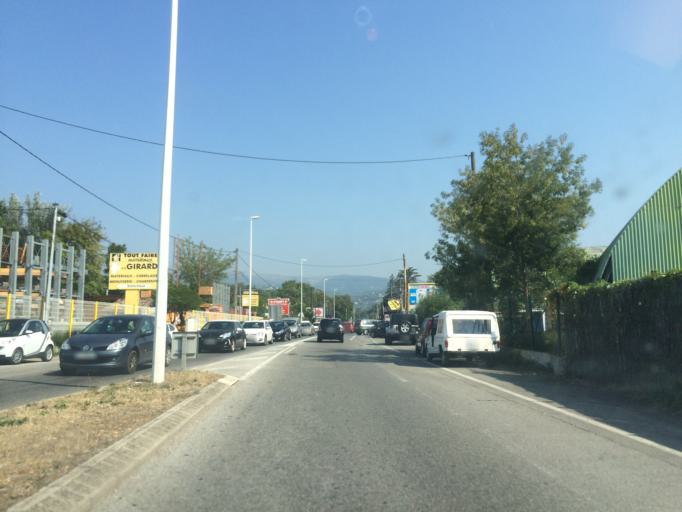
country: FR
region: Provence-Alpes-Cote d'Azur
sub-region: Departement des Alpes-Maritimes
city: Villeneuve-Loubet
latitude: 43.6710
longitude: 7.1247
